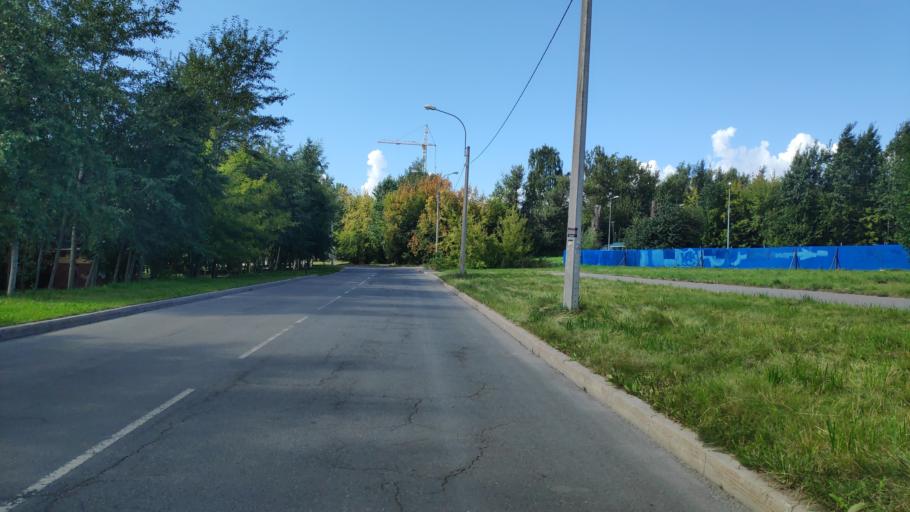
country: RU
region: St.-Petersburg
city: Krasnogvargeisky
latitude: 59.9337
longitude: 30.4261
